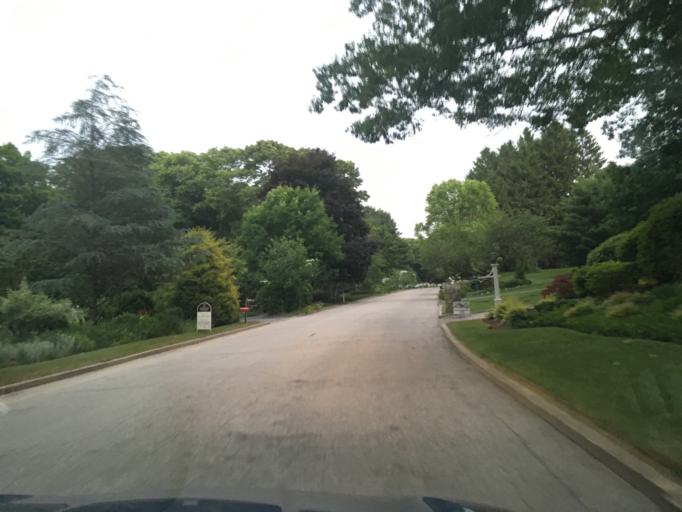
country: US
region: Rhode Island
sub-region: Washington County
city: Exeter
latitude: 41.6331
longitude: -71.5216
